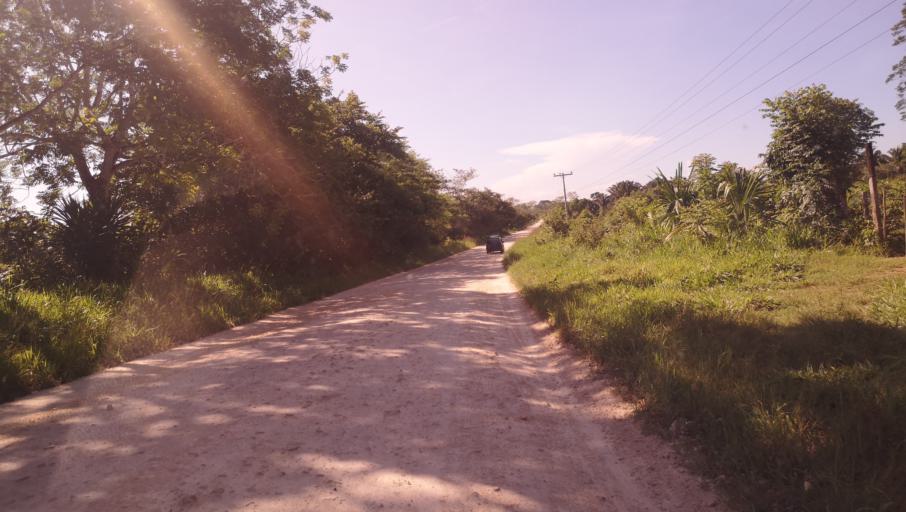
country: GT
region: Peten
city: Dolores
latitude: 16.7198
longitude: -89.3725
